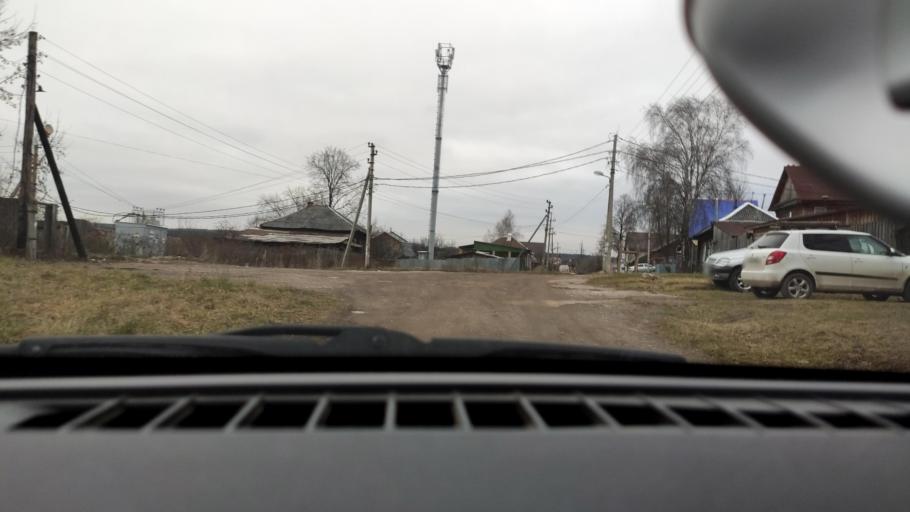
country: RU
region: Perm
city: Perm
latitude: 58.0281
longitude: 56.3362
